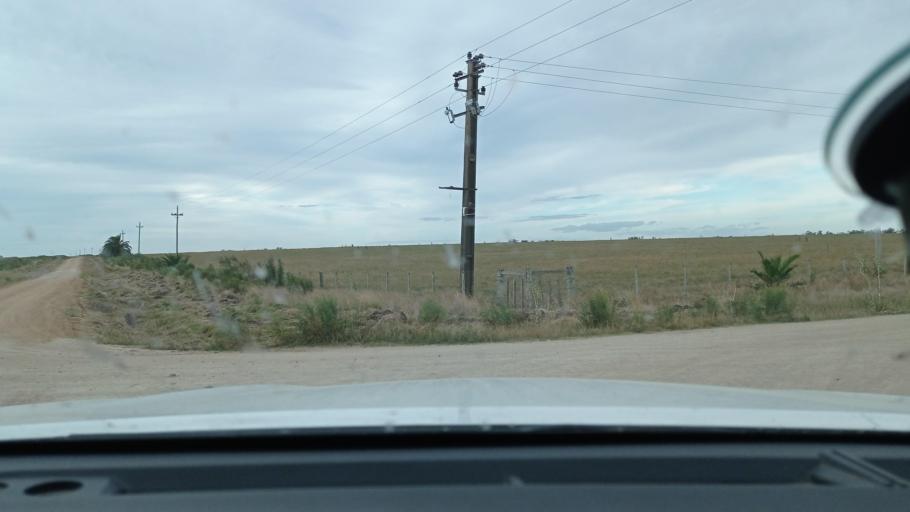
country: UY
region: Florida
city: Casupa
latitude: -34.1038
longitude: -55.7628
